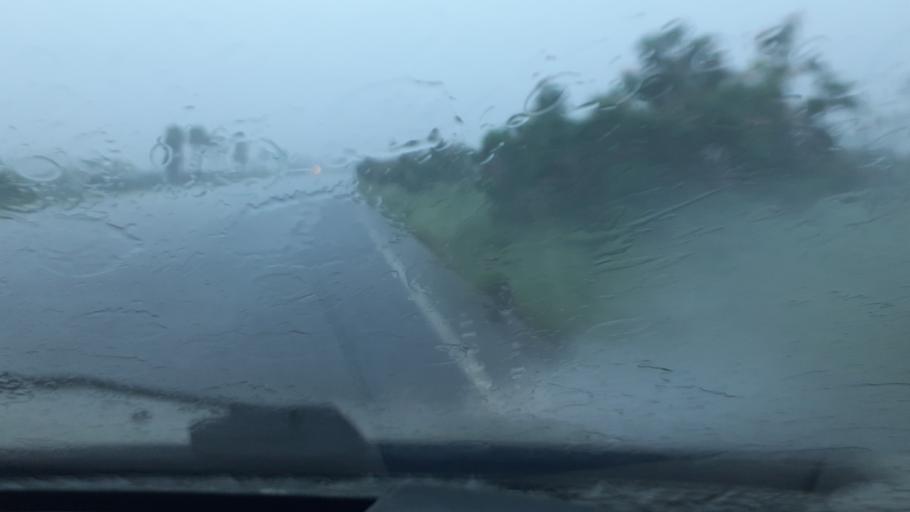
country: IN
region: Tamil Nadu
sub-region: Virudhunagar
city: Virudunagar
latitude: 9.4825
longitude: 77.9409
